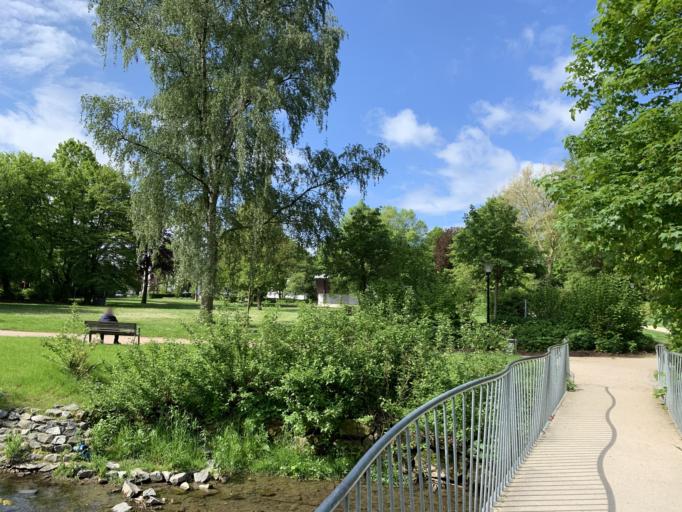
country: DE
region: North Rhine-Westphalia
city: Eslohe
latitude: 51.2566
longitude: 8.1704
